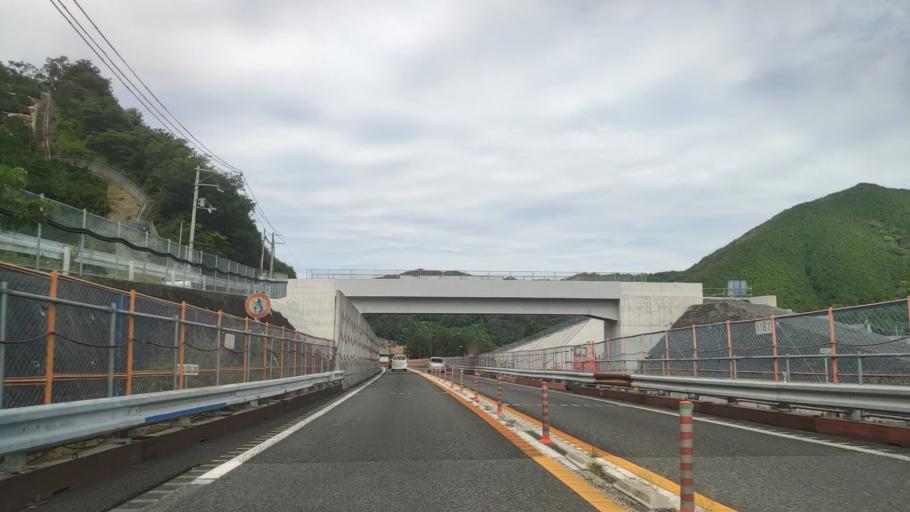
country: JP
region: Wakayama
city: Gobo
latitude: 33.9922
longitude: 135.1988
